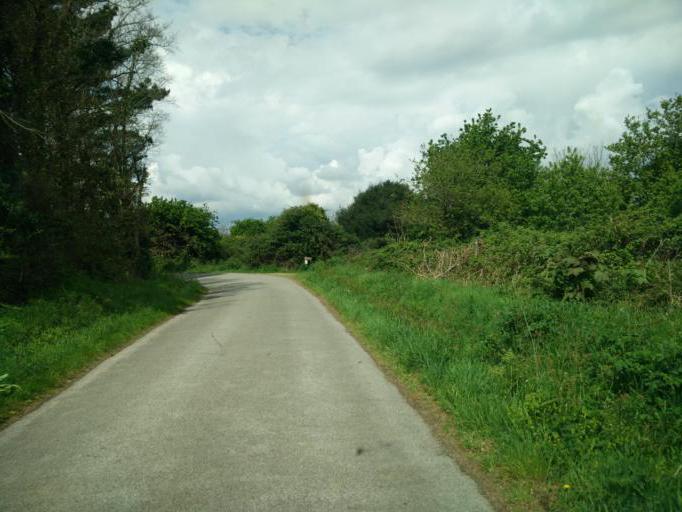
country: FR
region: Brittany
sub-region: Departement du Finistere
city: Roscanvel
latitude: 48.3367
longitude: -4.5515
